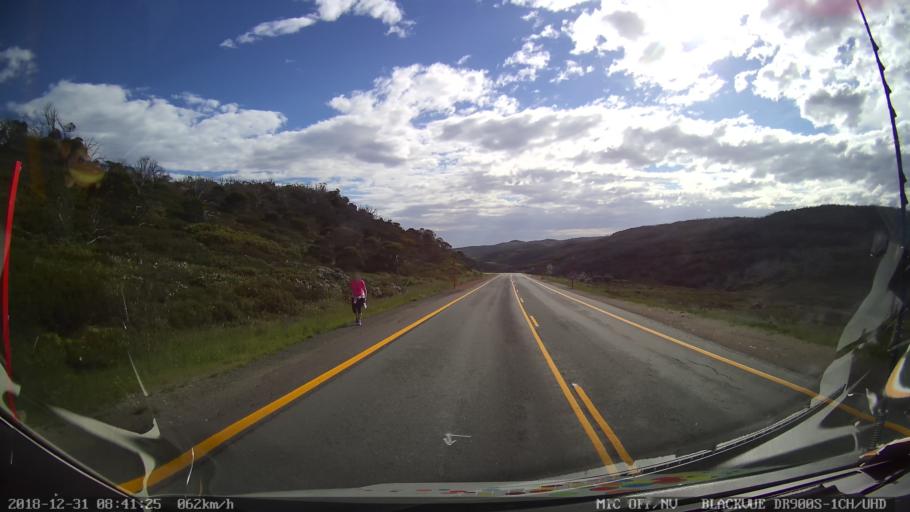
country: AU
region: New South Wales
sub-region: Snowy River
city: Jindabyne
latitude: -36.3981
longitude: 148.4218
